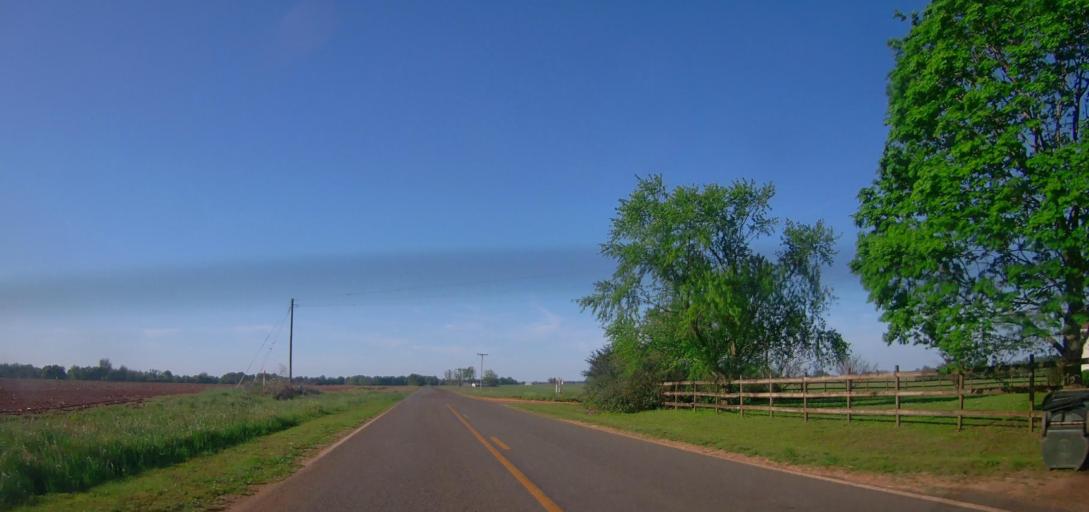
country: US
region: Georgia
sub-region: Macon County
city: Montezuma
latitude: 32.3412
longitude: -83.9439
